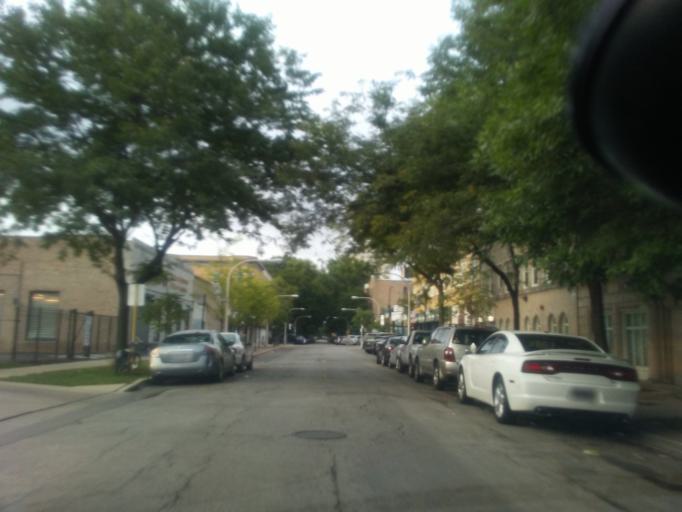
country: US
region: Illinois
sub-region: Cook County
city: Evanston
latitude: 41.9740
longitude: -87.6578
